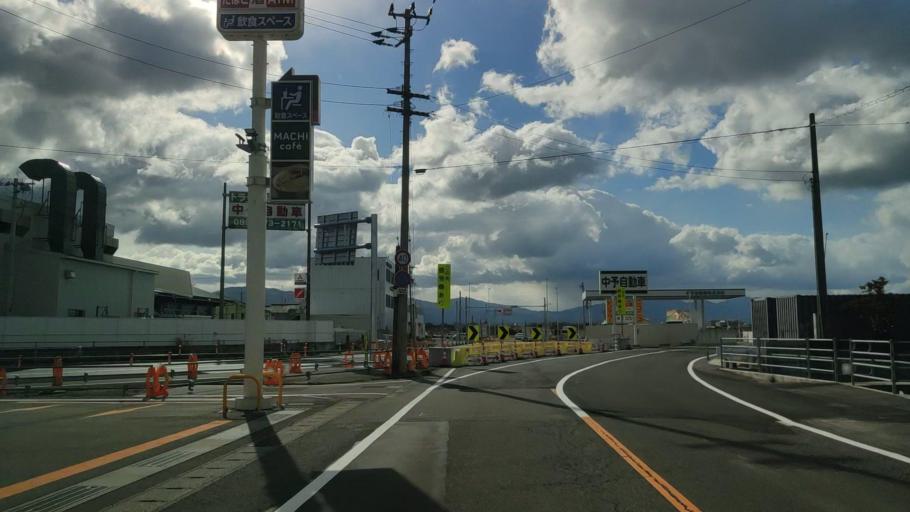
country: JP
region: Ehime
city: Masaki-cho
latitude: 33.8214
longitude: 132.7133
